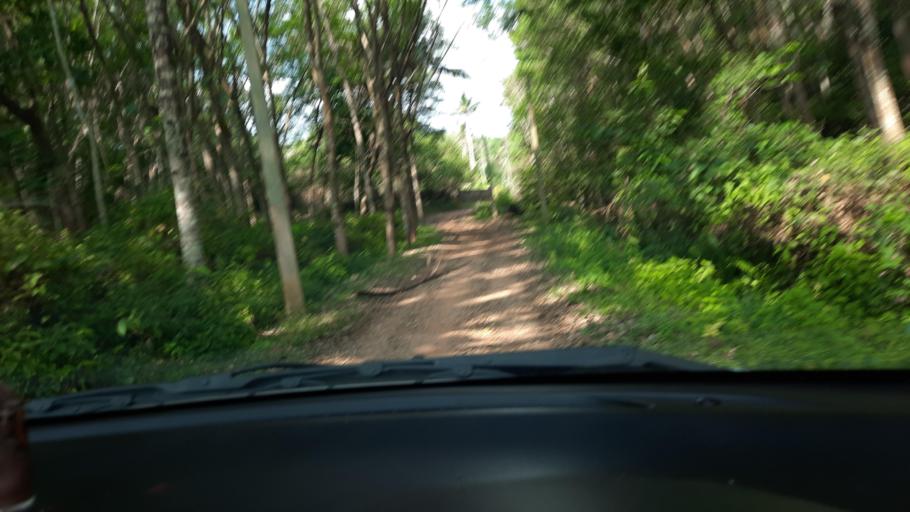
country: IN
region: Kerala
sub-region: Thiruvananthapuram
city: Nedumangad
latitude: 8.5936
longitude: 76.9260
